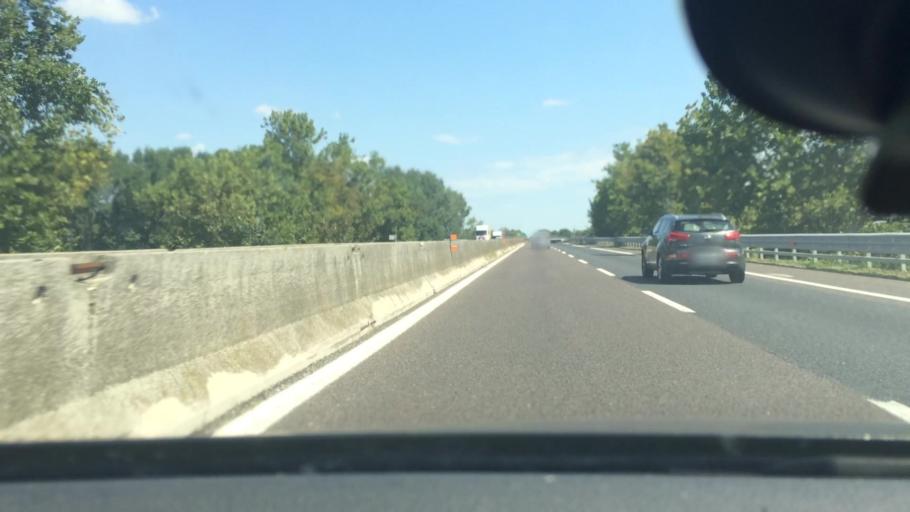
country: IT
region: Emilia-Romagna
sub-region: Provincia di Bologna
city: Malalbergo
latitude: 44.7138
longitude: 11.5007
